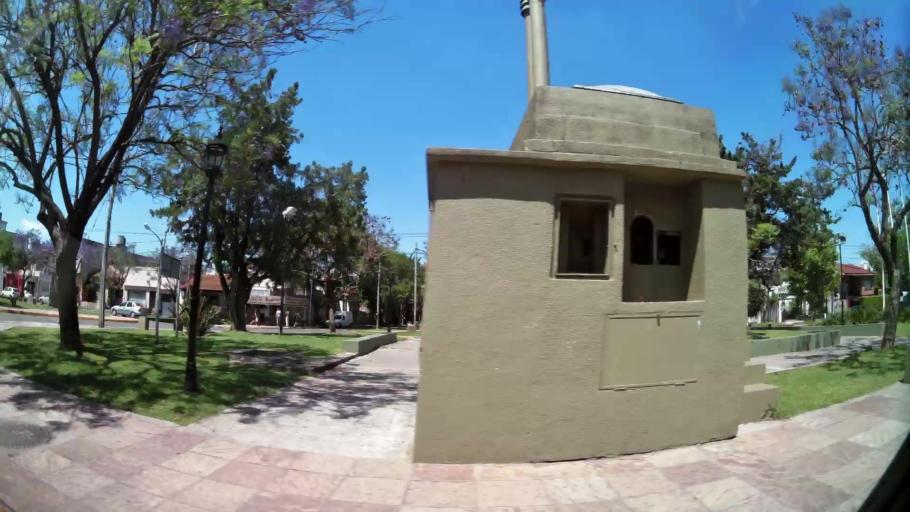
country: AR
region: Buenos Aires
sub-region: Partido de Tigre
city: Tigre
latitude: -34.4309
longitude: -58.5755
